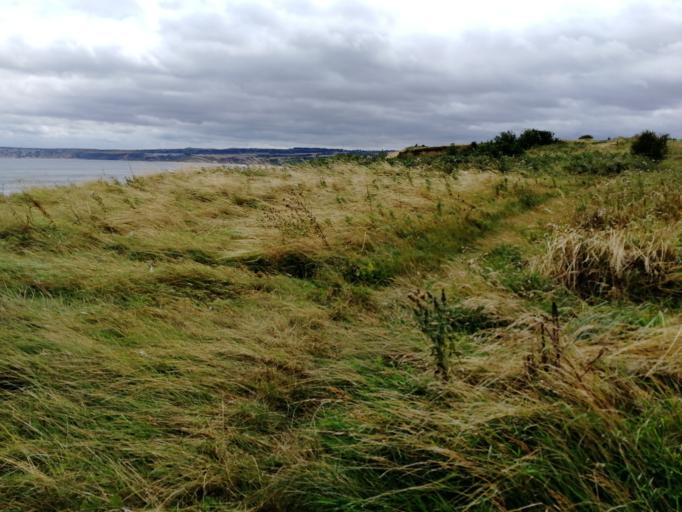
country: GB
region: England
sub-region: North Yorkshire
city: Filey
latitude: 54.2024
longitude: -0.2862
